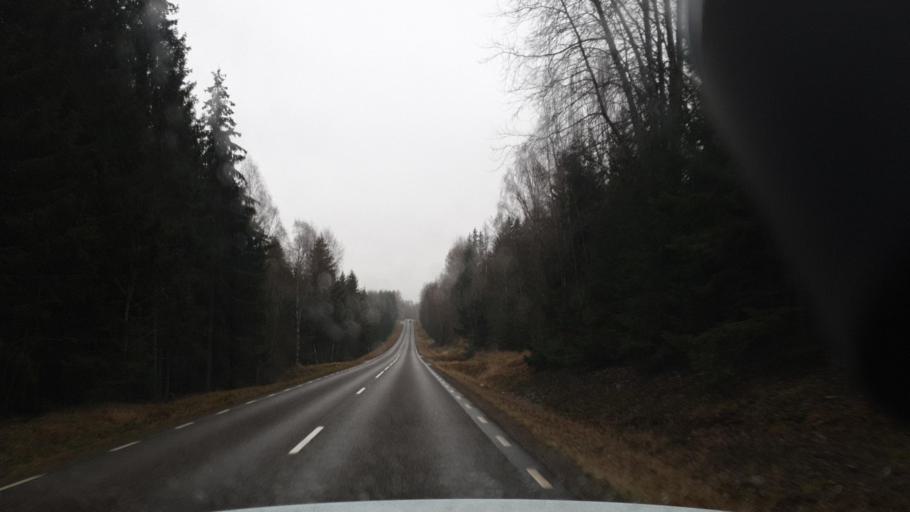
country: SE
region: Vaermland
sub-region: Eda Kommun
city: Amotfors
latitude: 59.7271
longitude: 12.4220
